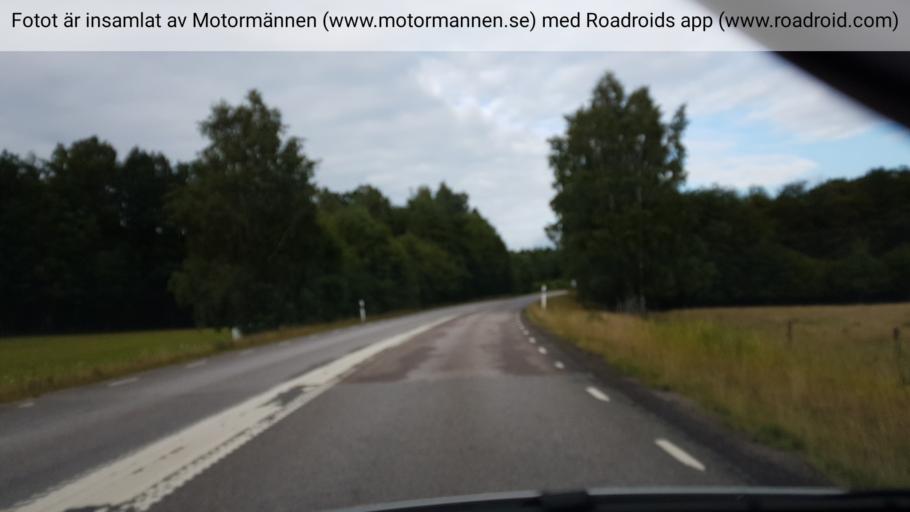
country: SE
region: Vaestra Goetaland
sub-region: Hjo Kommun
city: Hjo
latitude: 58.3215
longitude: 14.2705
